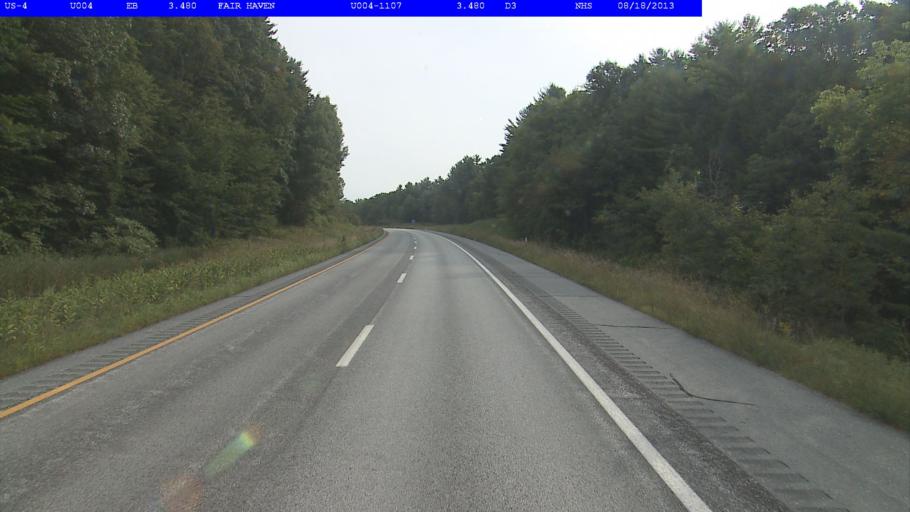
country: US
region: Vermont
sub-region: Rutland County
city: Fair Haven
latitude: 43.6060
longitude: -73.2424
